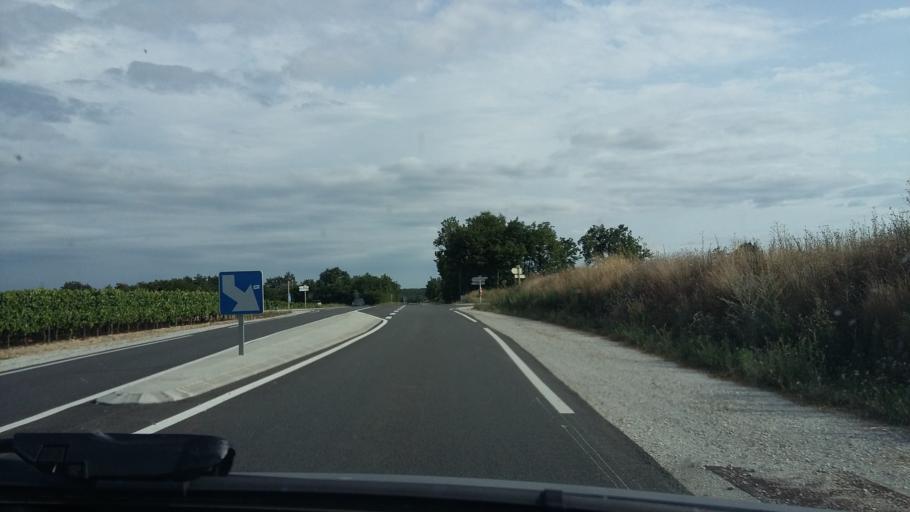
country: FR
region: Poitou-Charentes
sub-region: Departement de la Charente
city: Asnieres-sur-Nouere
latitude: 45.7311
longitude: 0.0633
